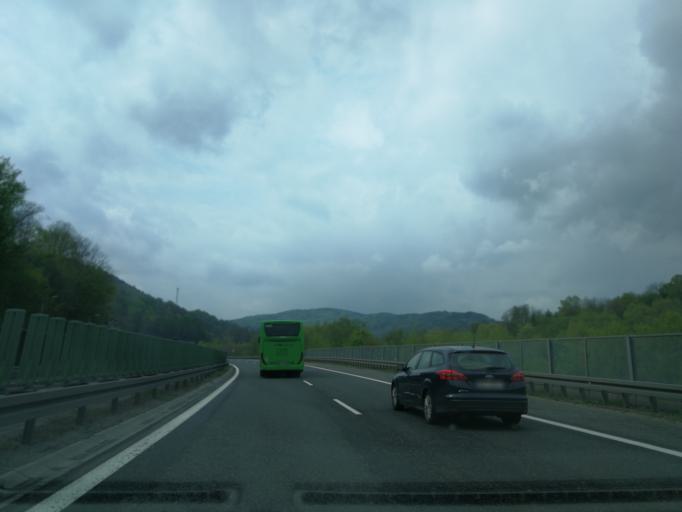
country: PL
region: Lesser Poland Voivodeship
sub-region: Powiat myslenicki
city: Stroza
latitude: 49.7879
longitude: 19.9371
